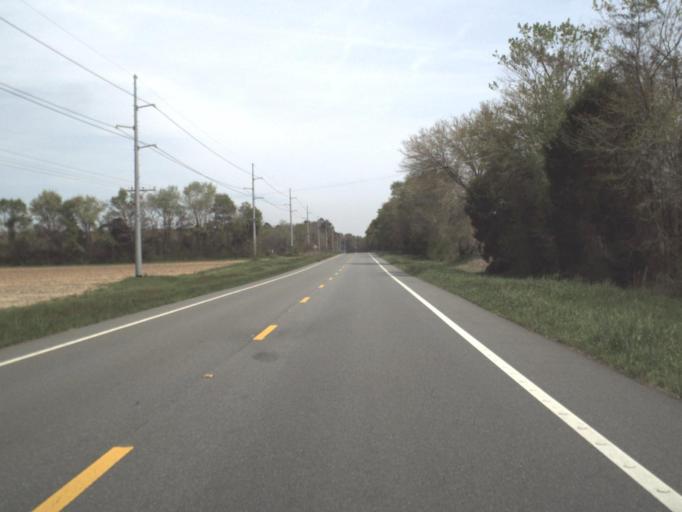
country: US
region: Alabama
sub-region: Houston County
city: Cottonwood
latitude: 30.9360
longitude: -85.3140
